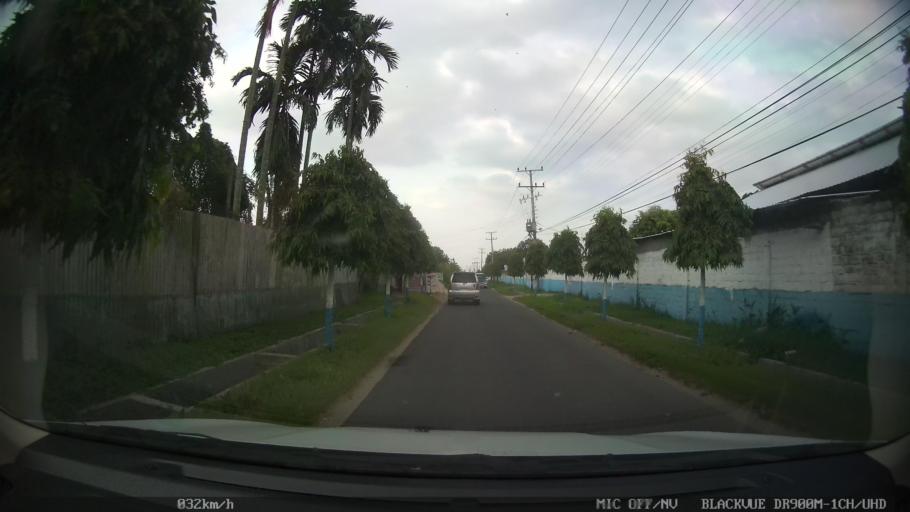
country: ID
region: North Sumatra
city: Sunggal
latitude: 3.5597
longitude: 98.5593
